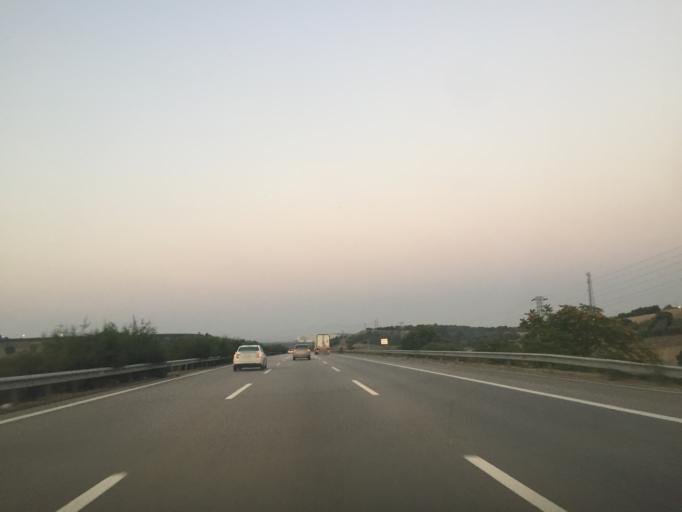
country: TR
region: Bursa
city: Gorukle
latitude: 40.2632
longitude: 28.8622
